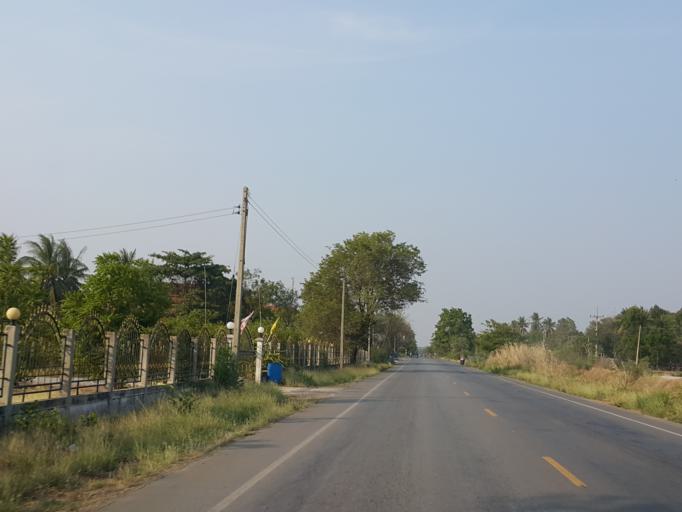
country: TH
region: Chai Nat
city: Sankhaburi
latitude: 15.0030
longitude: 100.1246
